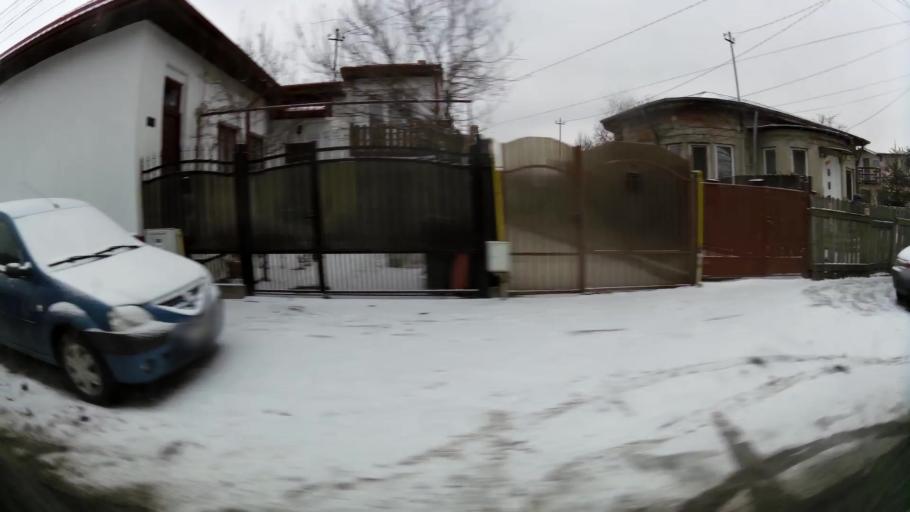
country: RO
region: Prahova
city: Ploiesti
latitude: 44.9364
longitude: 26.0367
